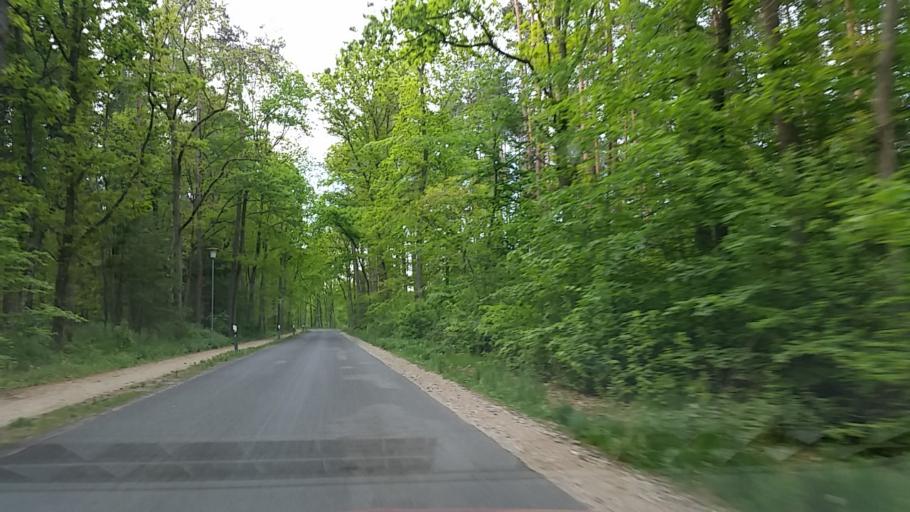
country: DE
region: Lower Saxony
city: Bodenteich
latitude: 52.8435
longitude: 10.6705
